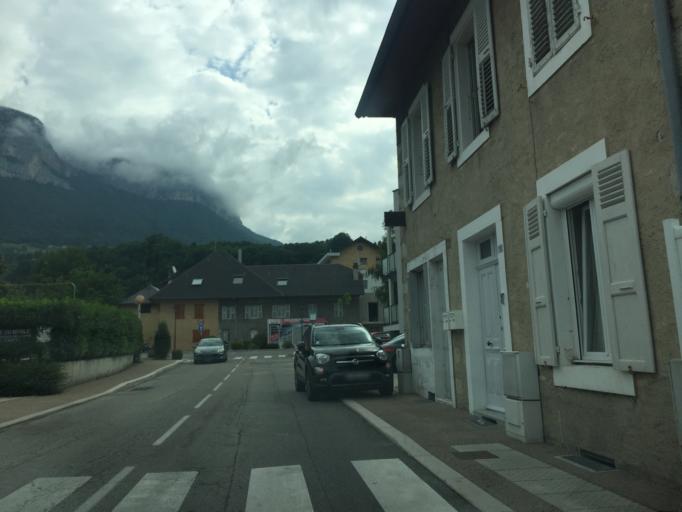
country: FR
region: Rhone-Alpes
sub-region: Departement de la Savoie
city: Barby
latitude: 45.5752
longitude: 5.9720
